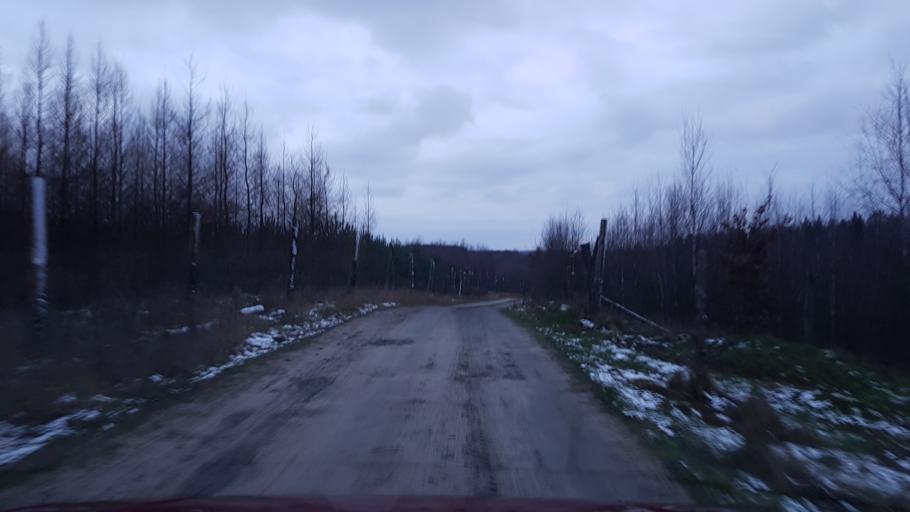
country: PL
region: Pomeranian Voivodeship
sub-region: Powiat bytowski
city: Tuchomie
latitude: 54.1469
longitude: 17.3025
